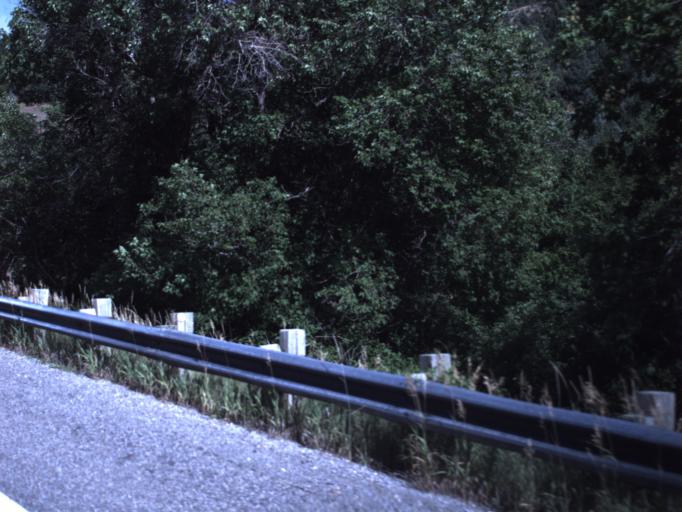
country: US
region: Utah
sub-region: Cache County
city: North Logan
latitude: 41.7742
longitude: -111.6530
